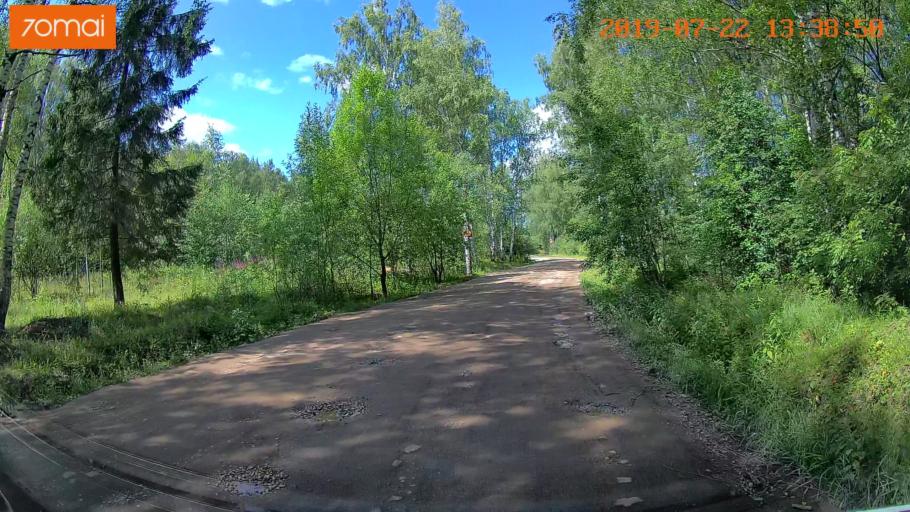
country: RU
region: Ivanovo
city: Novo-Talitsy
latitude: 57.0709
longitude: 40.8822
